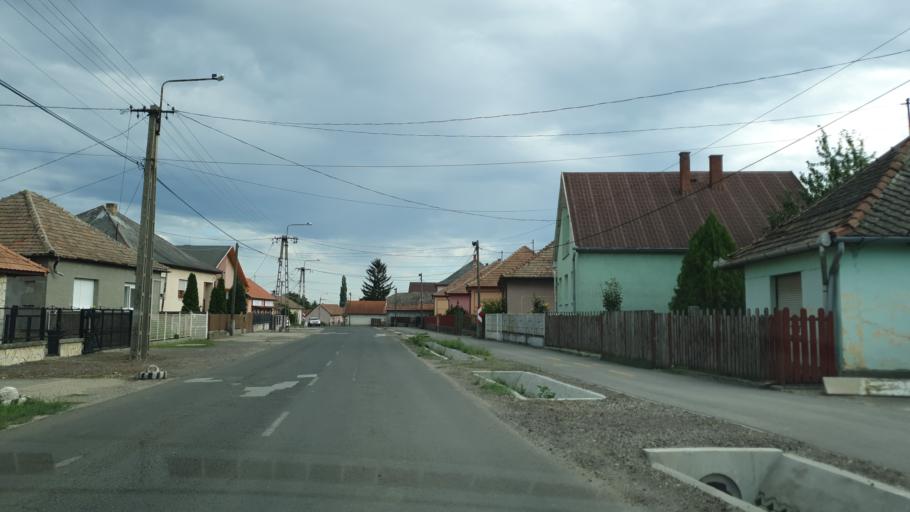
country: HU
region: Heves
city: Lorinci
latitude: 47.7530
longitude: 19.6791
